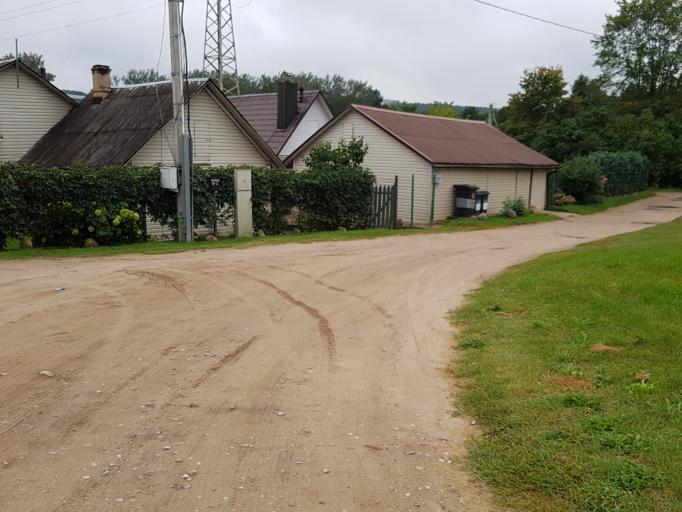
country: LT
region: Vilnius County
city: Lazdynai
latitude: 54.6507
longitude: 25.2074
